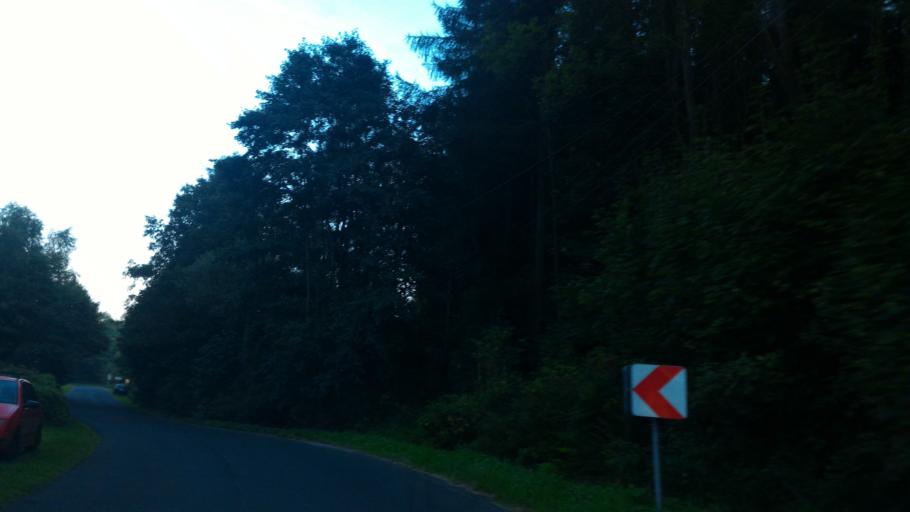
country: DE
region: Saxony
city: Kurort Jonsdorf
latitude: 50.8244
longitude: 14.6680
